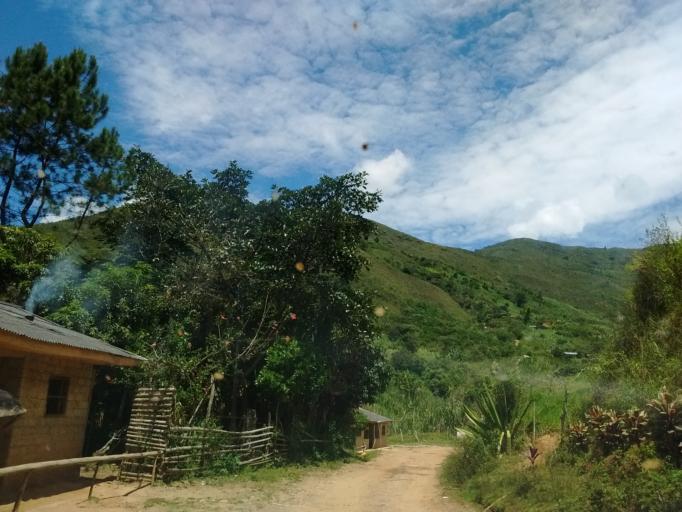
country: CO
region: Cauca
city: Villa Rica
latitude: 2.6535
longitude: -76.7699
